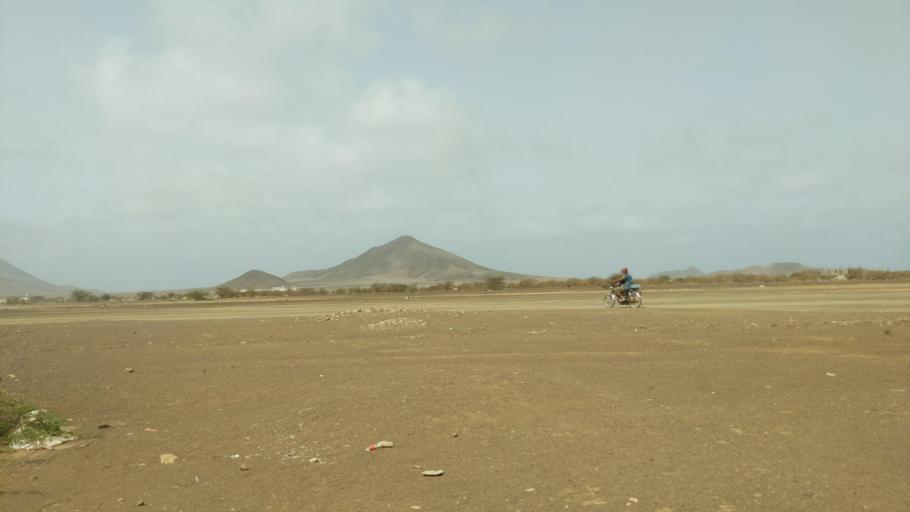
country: CV
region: Sal
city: Espargos
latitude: 16.7687
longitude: -22.9456
